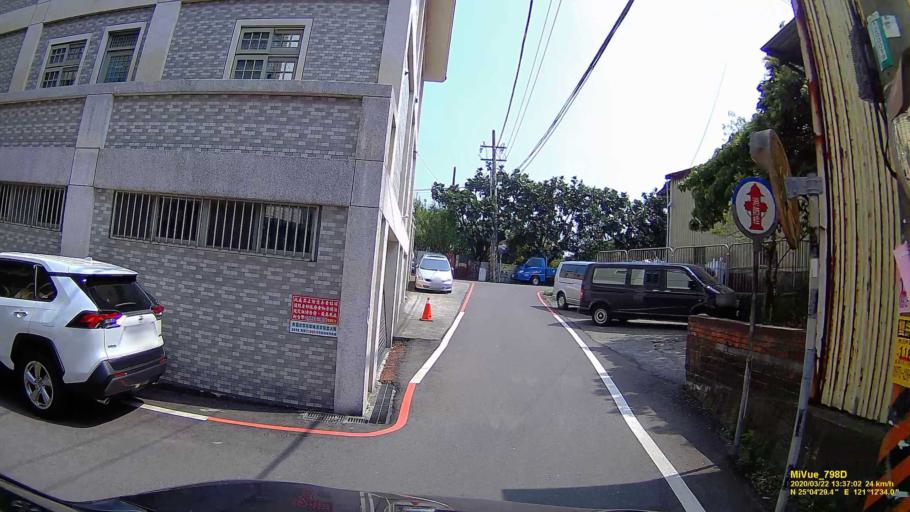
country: TW
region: Taiwan
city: Taoyuan City
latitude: 25.0747
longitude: 121.2095
